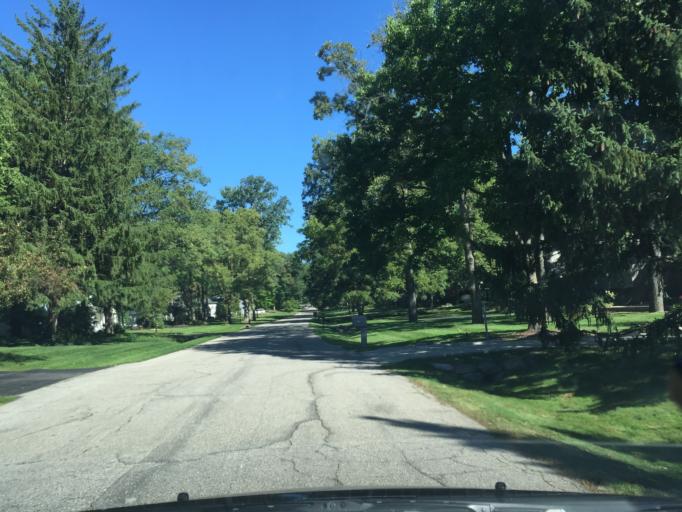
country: US
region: Michigan
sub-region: Oakland County
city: Franklin
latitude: 42.5628
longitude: -83.2910
